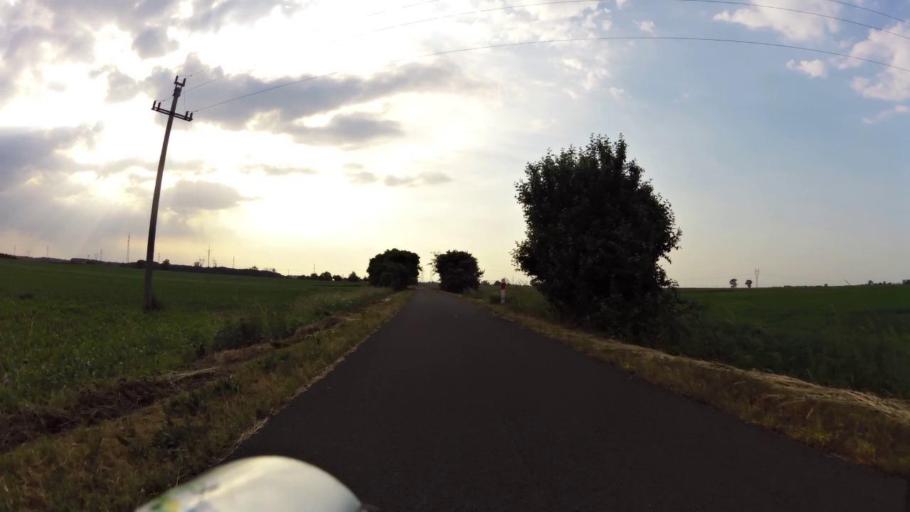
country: PL
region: Kujawsko-Pomorskie
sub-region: Powiat chelminski
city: Unislaw
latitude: 53.1787
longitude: 18.4095
